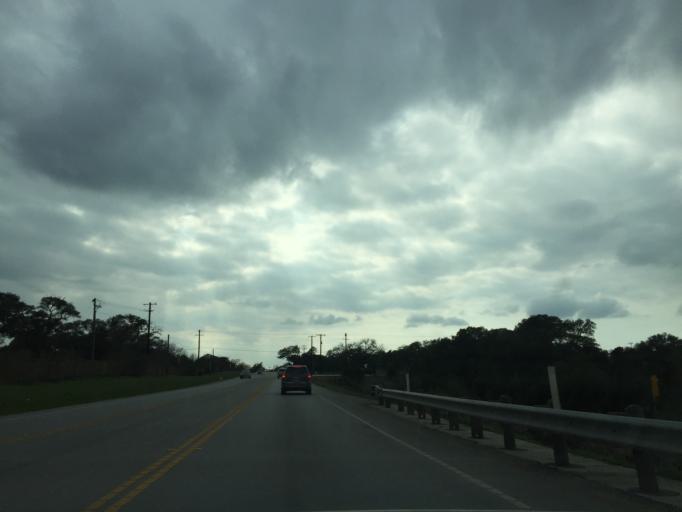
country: US
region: Texas
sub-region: Hays County
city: Dripping Springs
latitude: 30.1474
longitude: -97.9846
